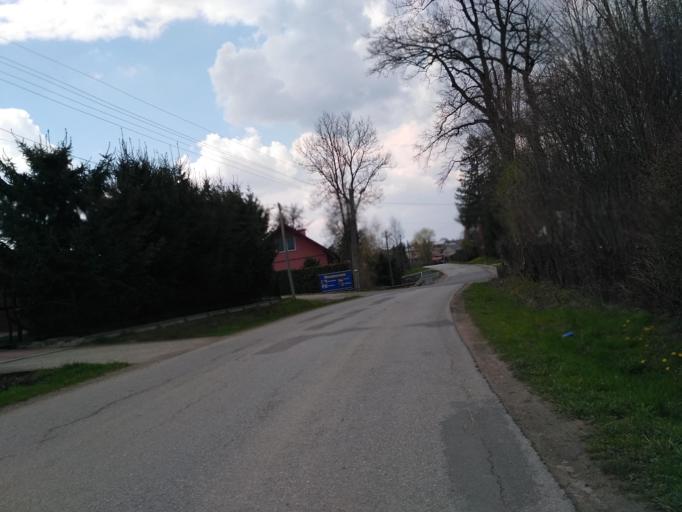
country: PL
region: Subcarpathian Voivodeship
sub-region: Powiat sanocki
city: Strachocina
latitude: 49.6096
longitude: 22.0780
